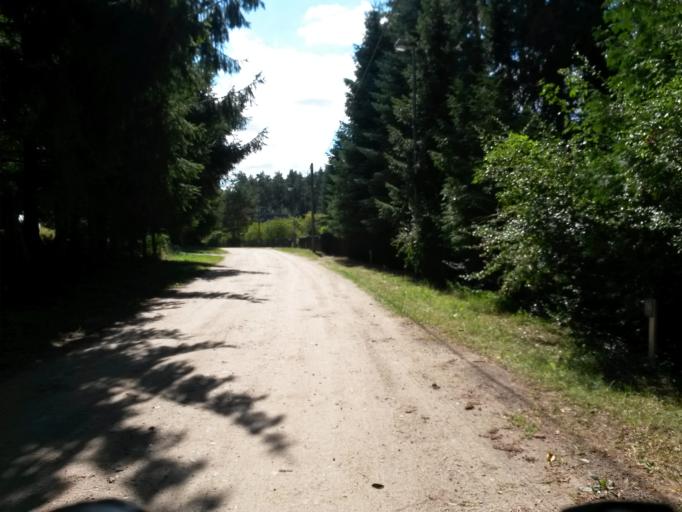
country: DE
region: Brandenburg
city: Milmersdorf
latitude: 53.1553
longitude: 13.5966
